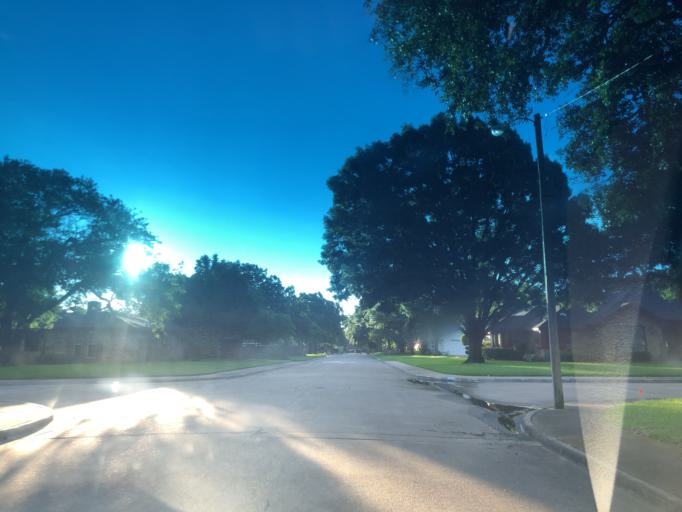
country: US
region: Texas
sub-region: Dallas County
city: Grand Prairie
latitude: 32.7817
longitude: -97.0360
